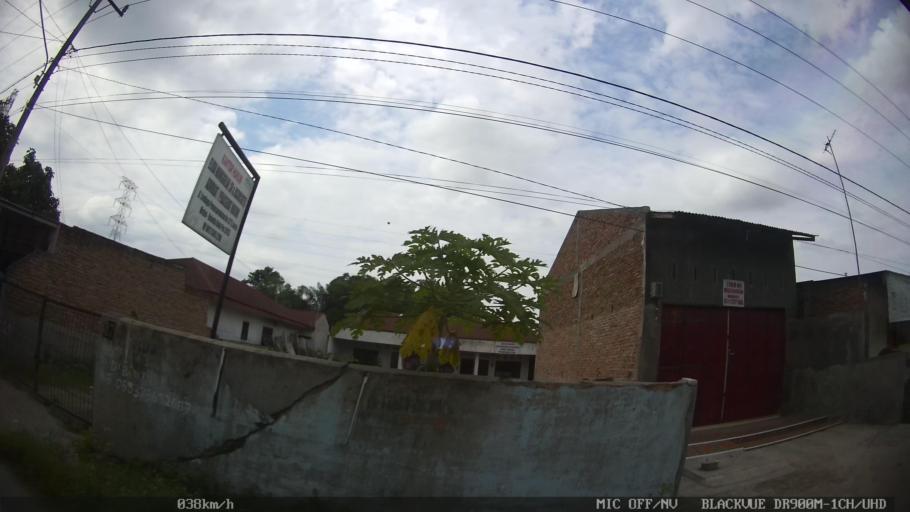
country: ID
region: North Sumatra
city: Sunggal
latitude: 3.6186
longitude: 98.6088
